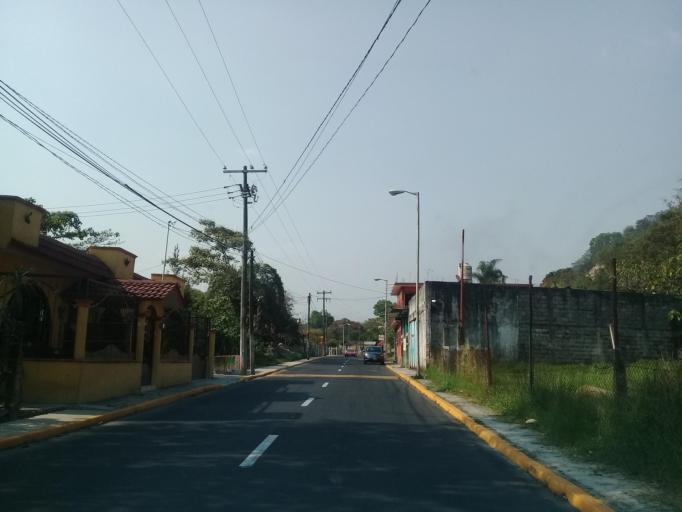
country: MX
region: Veracruz
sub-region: Ixtaczoquitlan
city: Campo Chico
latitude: 18.8477
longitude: -97.0366
